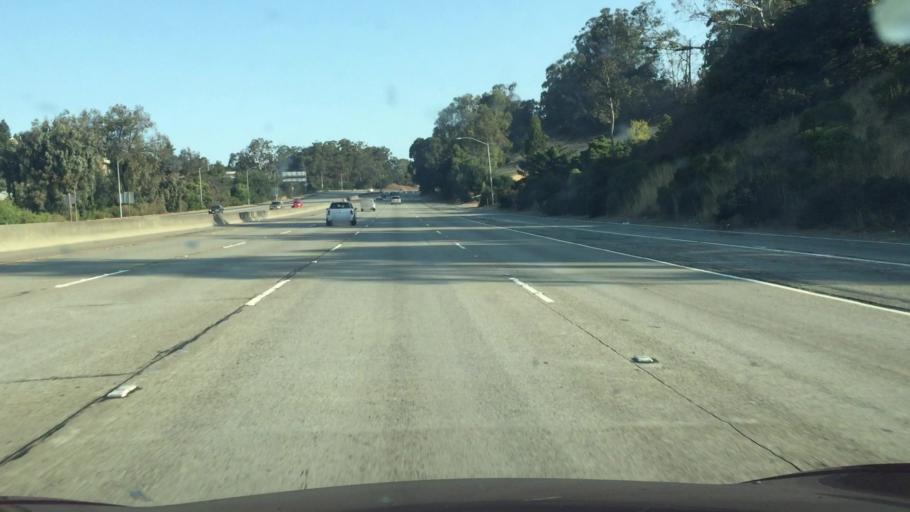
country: US
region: California
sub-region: Alameda County
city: San Leandro
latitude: 37.7470
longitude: -122.1498
